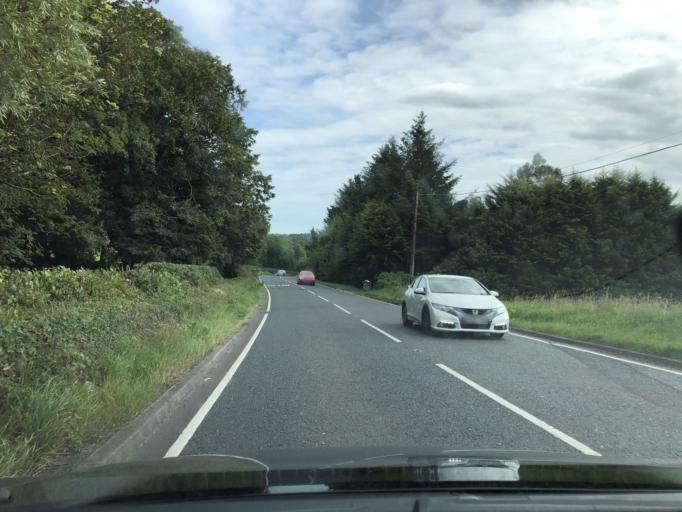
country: GB
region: Northern Ireland
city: Ballynahinch
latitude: 54.3627
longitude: -5.8593
